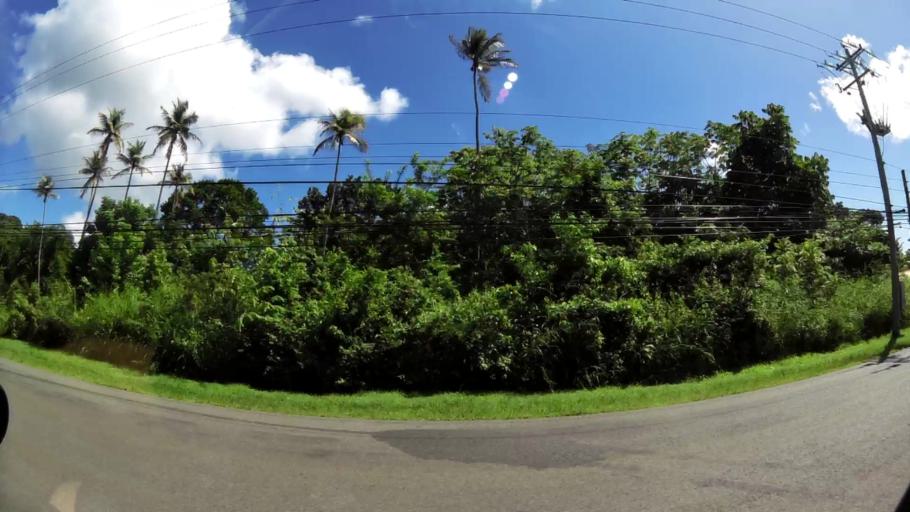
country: TT
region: Tobago
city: Scarborough
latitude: 11.1979
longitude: -60.7930
